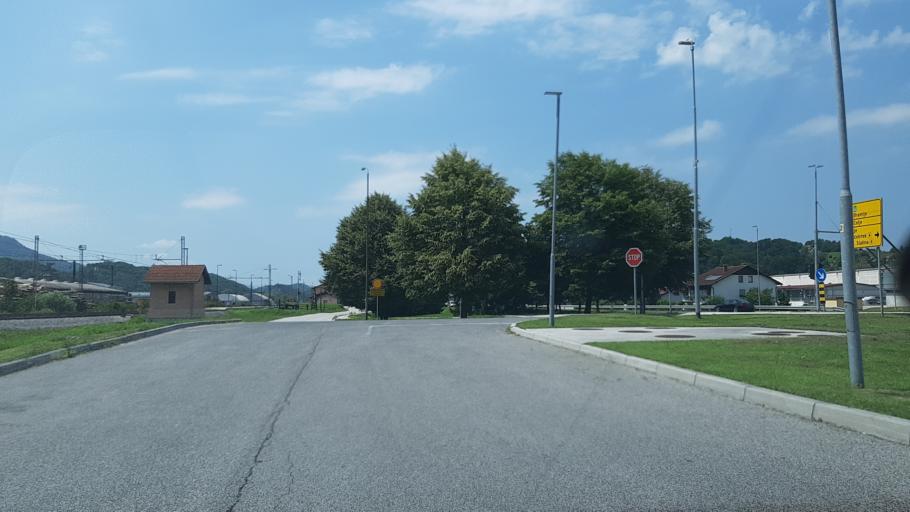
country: SI
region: Sentjur pri Celju
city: Sentjur
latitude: 46.2129
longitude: 15.3998
